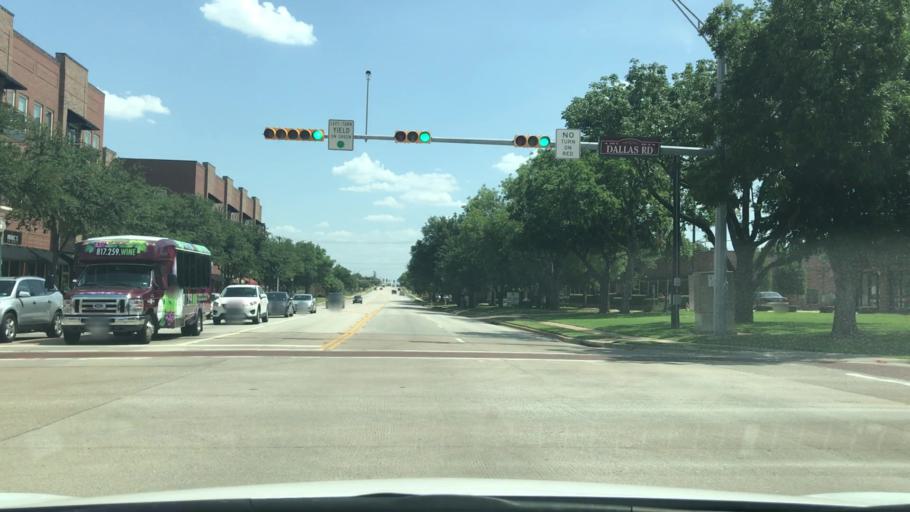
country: US
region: Texas
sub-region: Tarrant County
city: Grapevine
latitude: 32.9328
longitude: -97.0784
